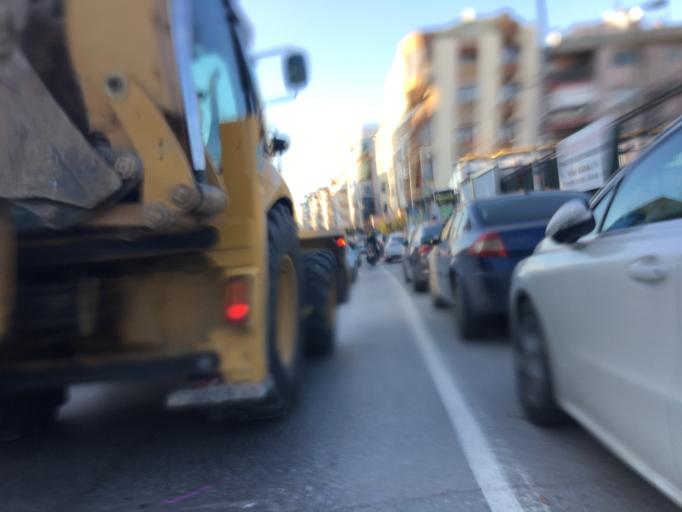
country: TR
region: Izmir
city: Buca
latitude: 38.3868
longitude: 27.1643
